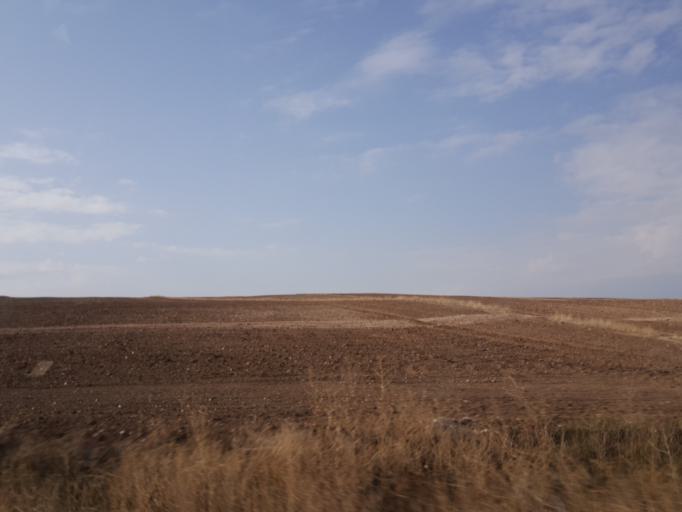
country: TR
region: Corum
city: Cemilbey
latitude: 40.1731
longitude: 35.0453
